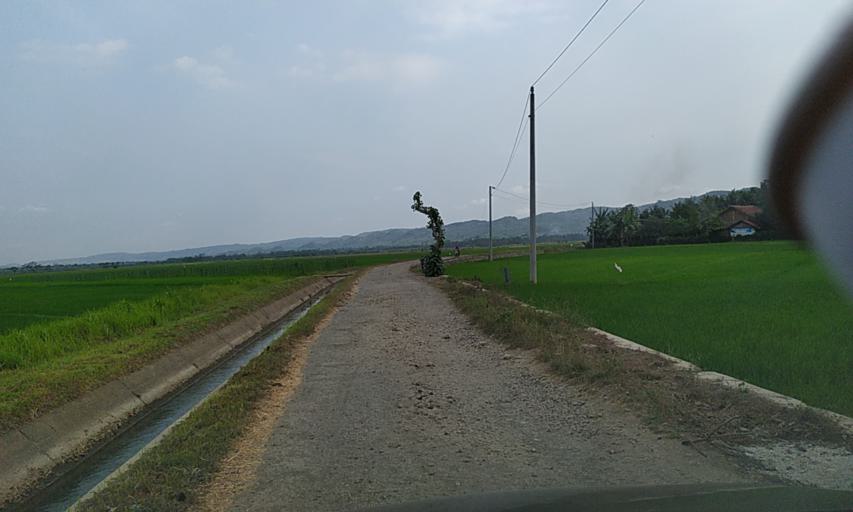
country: ID
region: Central Java
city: Mulyadadi
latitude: -7.3391
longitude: 108.7555
